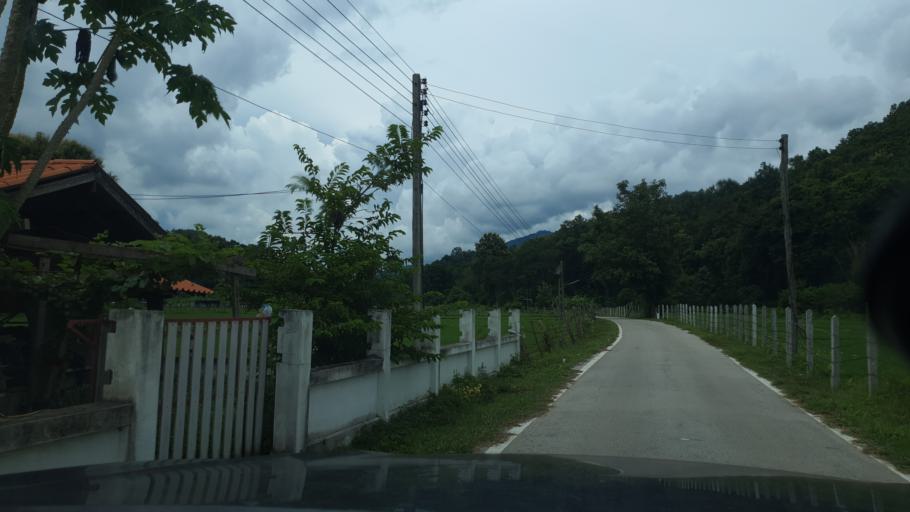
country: TH
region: Lampang
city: Hang Chat
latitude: 18.4311
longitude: 99.2680
